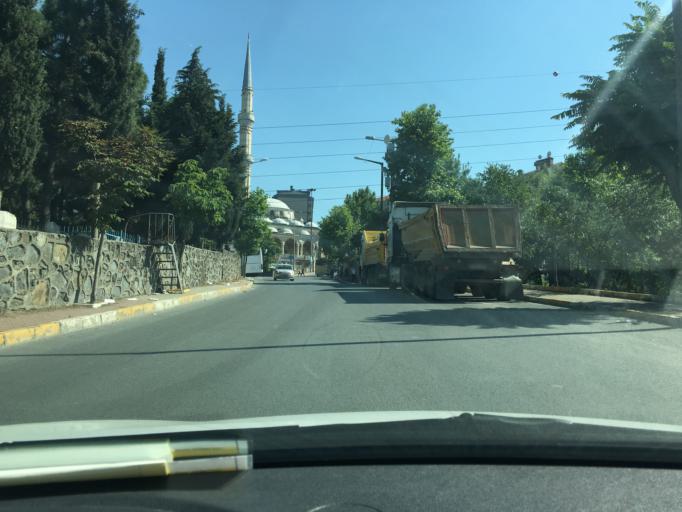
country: TR
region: Istanbul
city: Sisli
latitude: 41.0831
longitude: 28.9444
